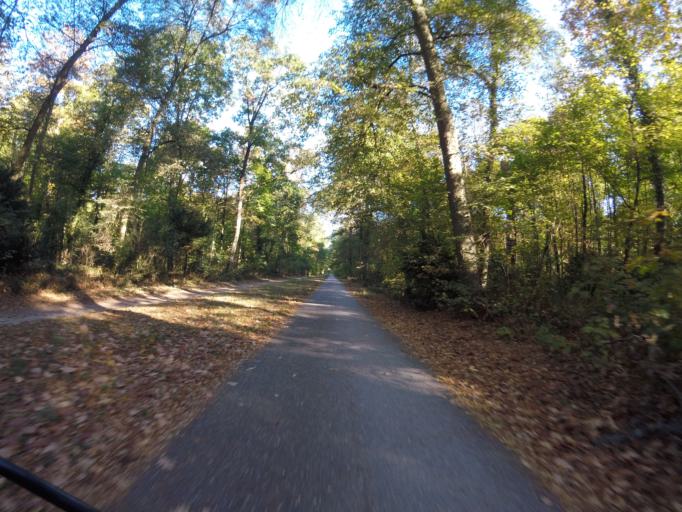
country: DE
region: Baden-Wuerttemberg
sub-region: Karlsruhe Region
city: Karlsruhe
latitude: 49.0186
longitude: 8.4050
